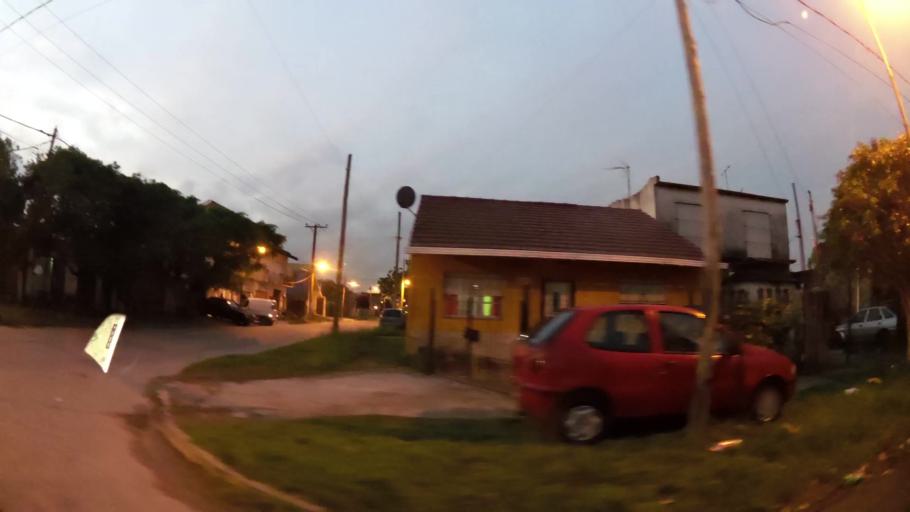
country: AR
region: Buenos Aires
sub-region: Partido de Lomas de Zamora
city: Lomas de Zamora
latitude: -34.7467
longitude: -58.3606
